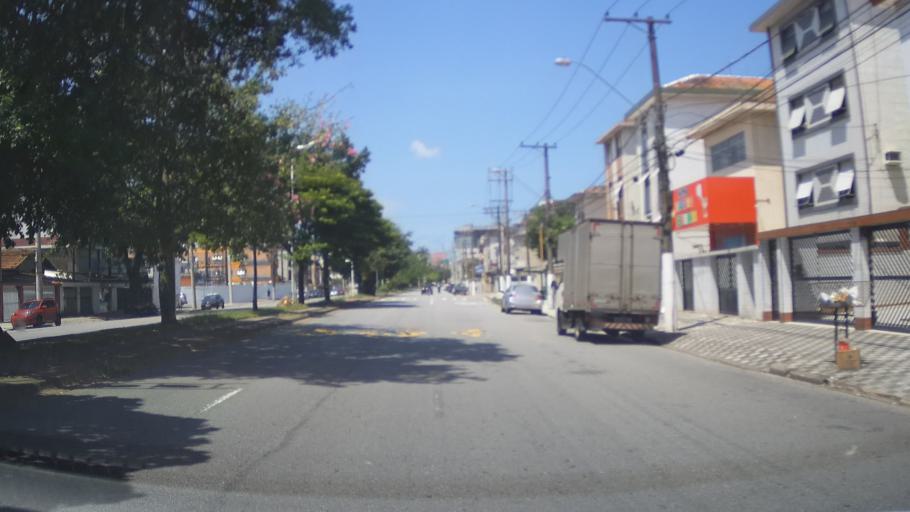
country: BR
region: Sao Paulo
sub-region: Santos
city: Santos
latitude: -23.9744
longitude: -46.3013
